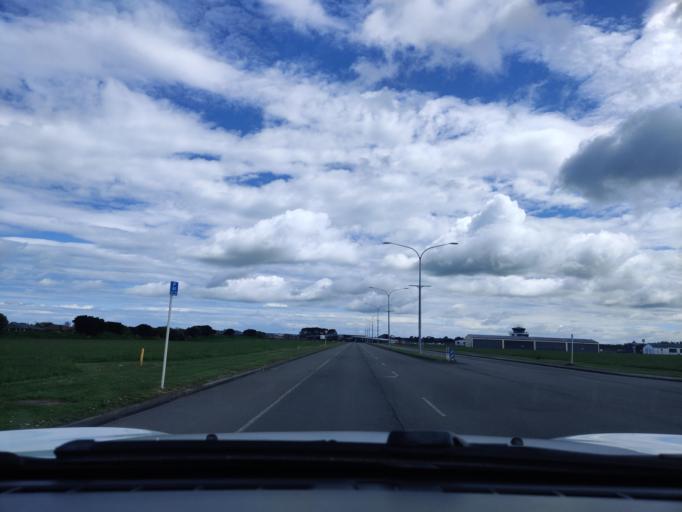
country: NZ
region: Manawatu-Wanganui
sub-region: Palmerston North City
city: Palmerston North
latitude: -40.3262
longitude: 175.6167
